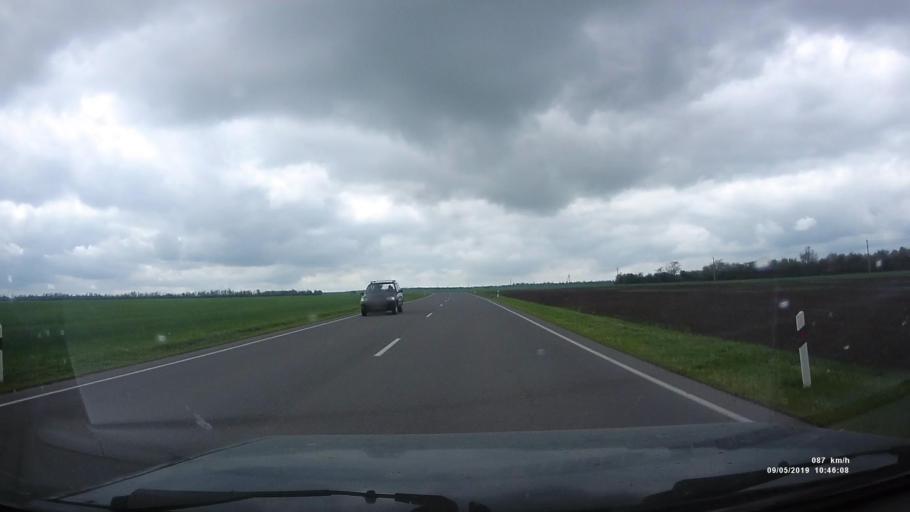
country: RU
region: Rostov
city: Peshkovo
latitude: 46.9881
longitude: 39.3583
